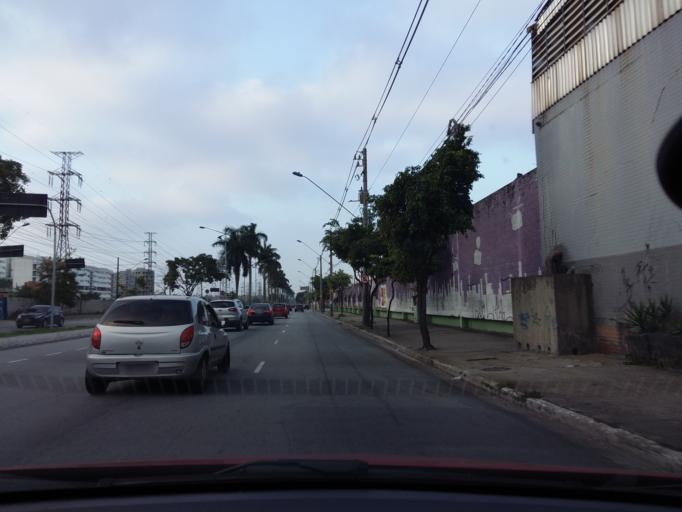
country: BR
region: Sao Paulo
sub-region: Sao Caetano Do Sul
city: Sao Caetano do Sul
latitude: -23.6212
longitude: -46.5816
